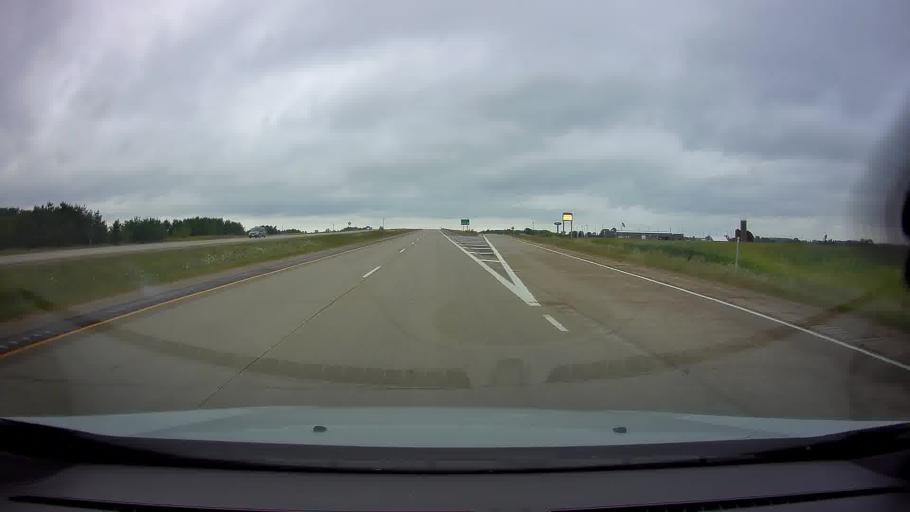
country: US
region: Wisconsin
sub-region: Brown County
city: Pulaski
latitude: 44.6694
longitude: -88.3070
